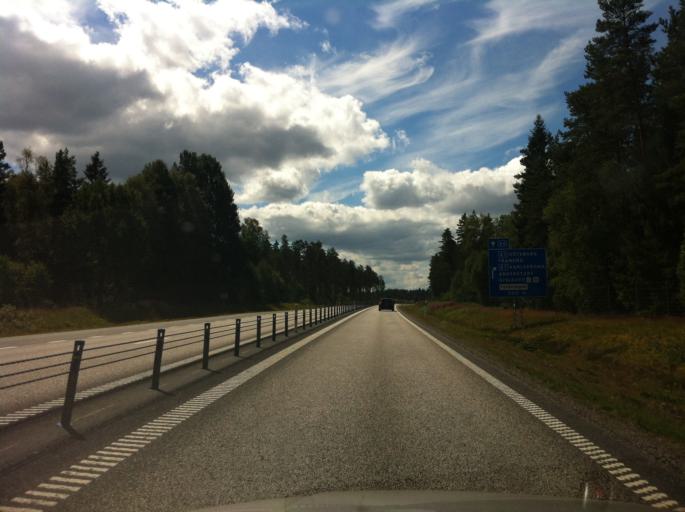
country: SE
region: Joenkoeping
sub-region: Gislaveds Kommun
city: Gislaved
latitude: 57.3366
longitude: 13.5488
